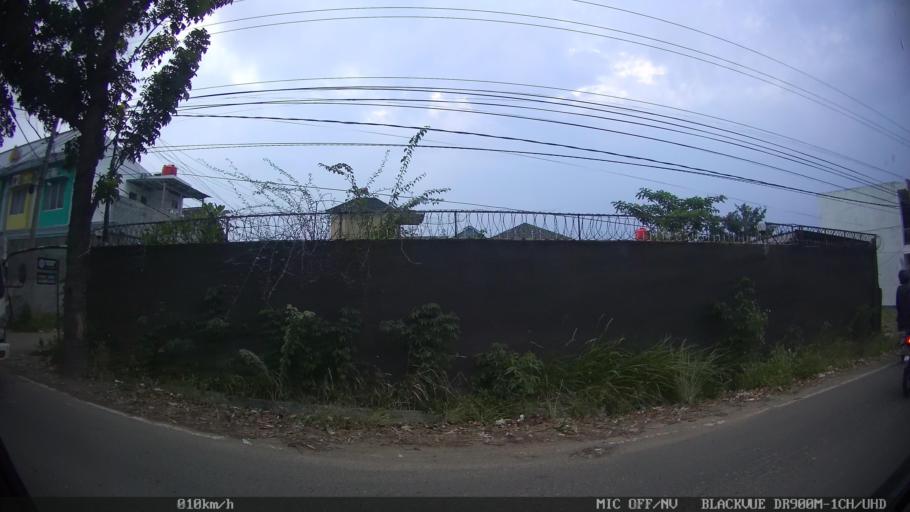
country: ID
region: Lampung
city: Bandarlampung
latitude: -5.4074
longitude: 105.2887
